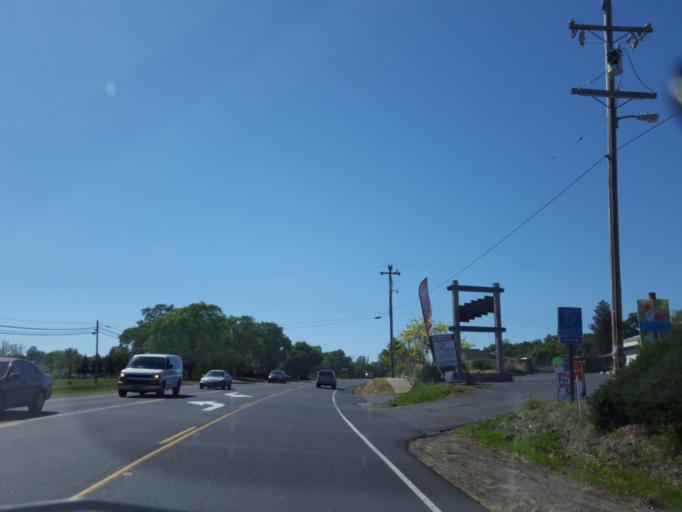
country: US
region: California
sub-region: Calaveras County
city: Angels Camp
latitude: 38.0857
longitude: -120.5662
